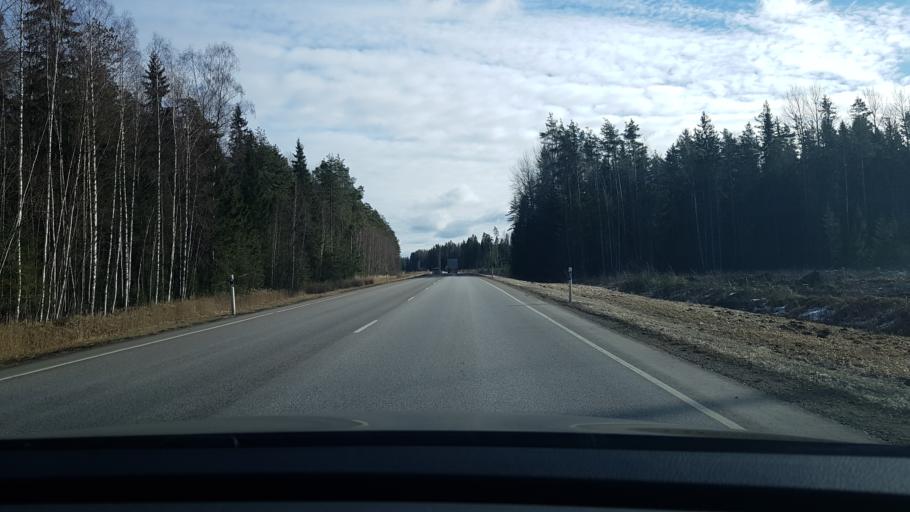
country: EE
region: Paernumaa
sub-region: Saarde vald
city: Kilingi-Nomme
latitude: 58.1668
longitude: 24.8245
